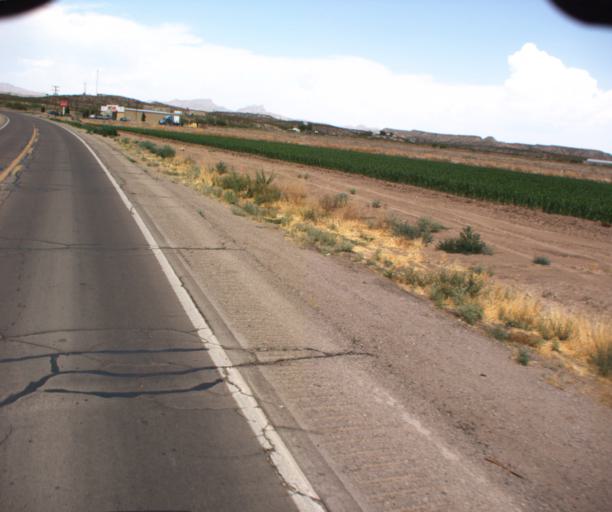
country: US
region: Arizona
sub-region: Greenlee County
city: Clifton
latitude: 32.7274
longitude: -109.0954
